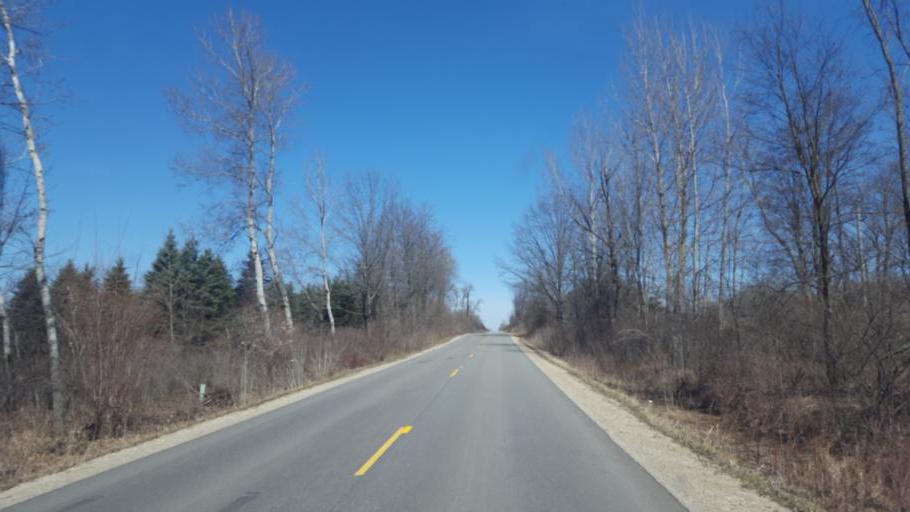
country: US
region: Michigan
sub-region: Montcalm County
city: Edmore
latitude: 43.5051
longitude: -85.1053
